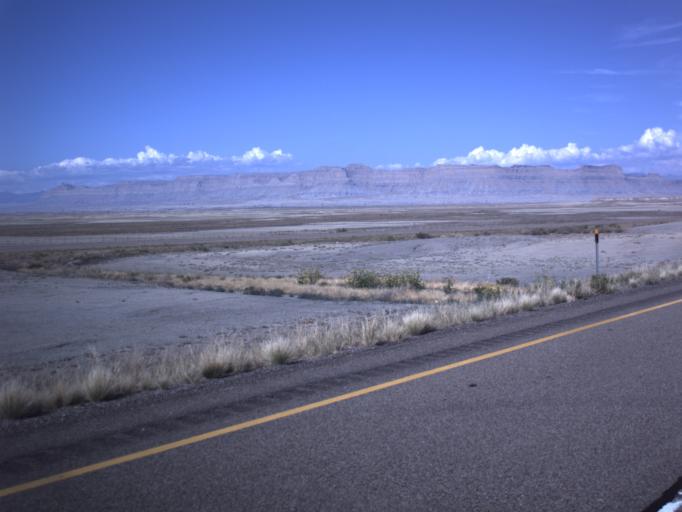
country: US
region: Utah
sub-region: Carbon County
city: East Carbon City
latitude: 38.9493
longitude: -110.3181
